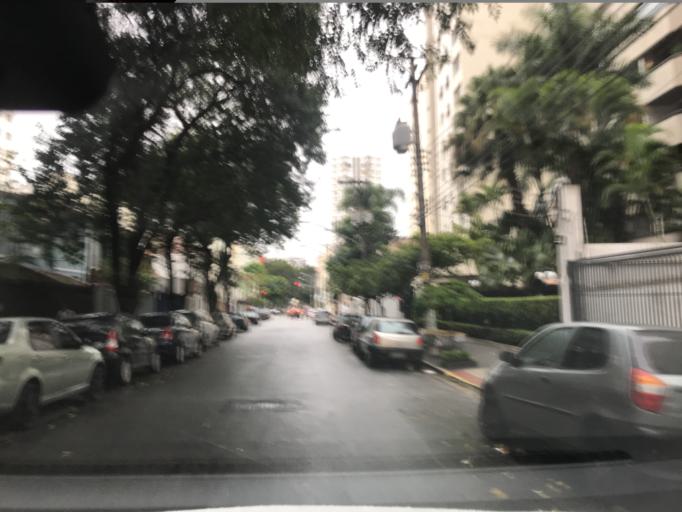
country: BR
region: Sao Paulo
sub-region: Sao Paulo
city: Sao Paulo
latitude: -23.5334
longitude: -46.6815
